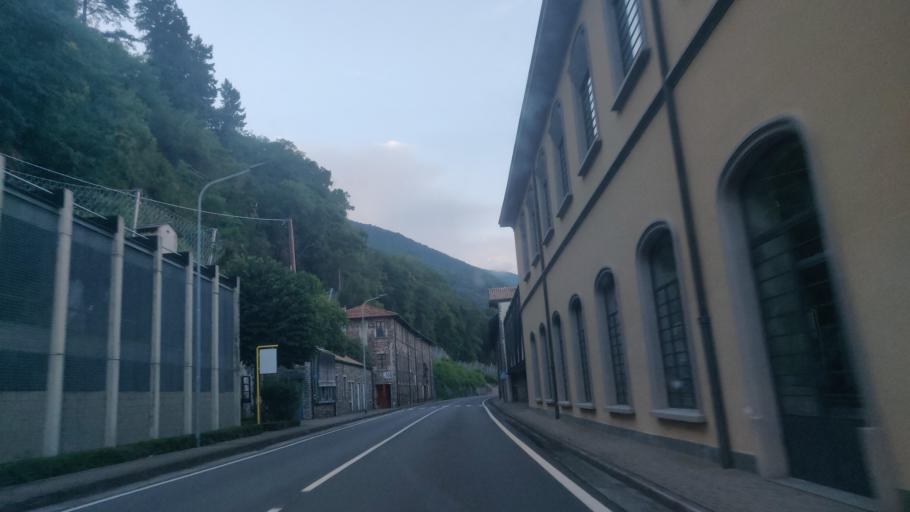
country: IT
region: Piedmont
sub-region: Provincia Verbano-Cusio-Ossola
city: Ghiffa
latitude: 45.9613
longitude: 8.6218
